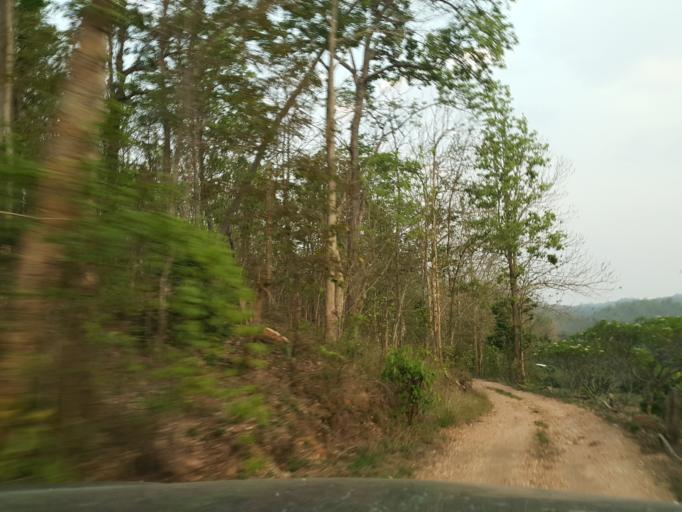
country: TH
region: Lamphun
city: Thung Hua Chang
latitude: 17.8976
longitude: 99.0834
